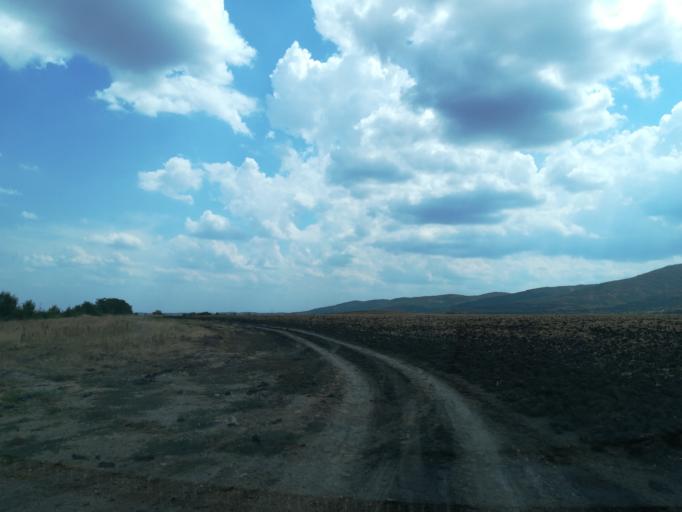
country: BG
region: Khaskovo
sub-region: Obshtina Mineralni Bani
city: Mineralni Bani
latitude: 41.9991
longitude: 25.1882
